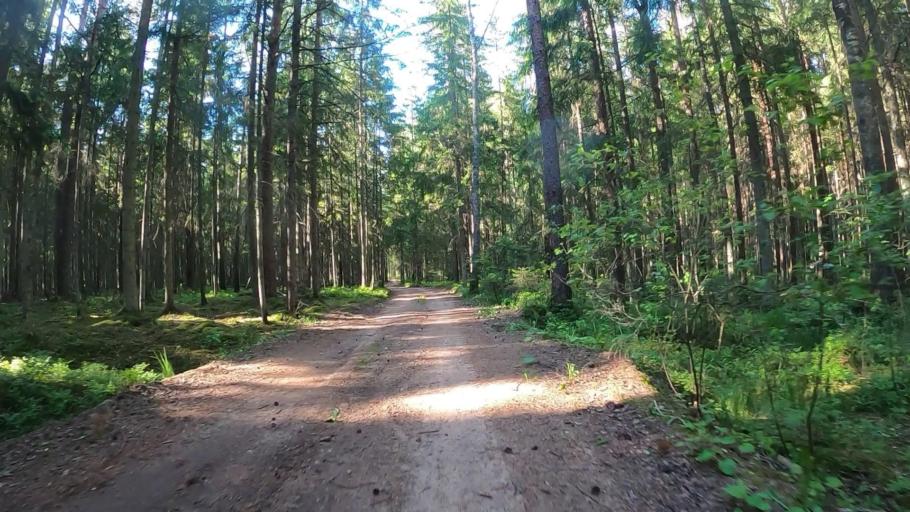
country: LV
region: Ogre
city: Ogre
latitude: 56.8368
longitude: 24.5902
